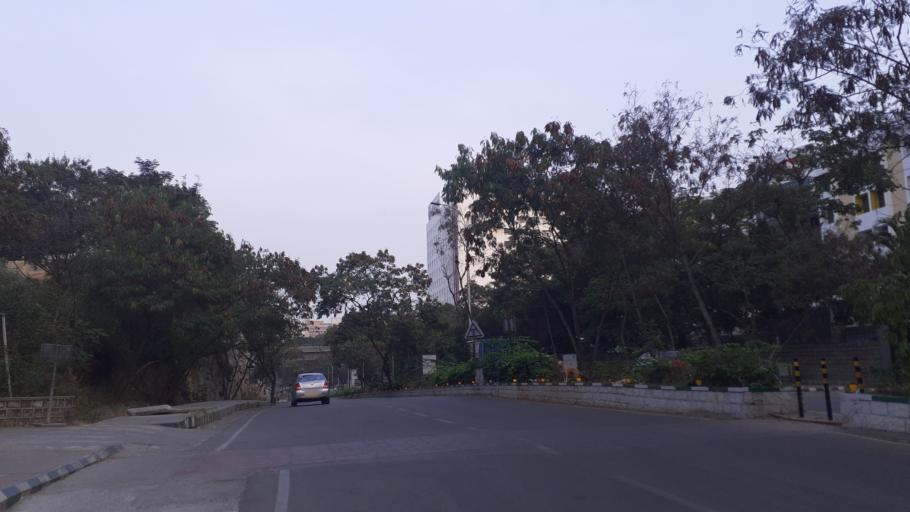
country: IN
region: Telangana
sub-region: Rangareddi
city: Kukatpalli
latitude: 17.4440
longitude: 78.3749
